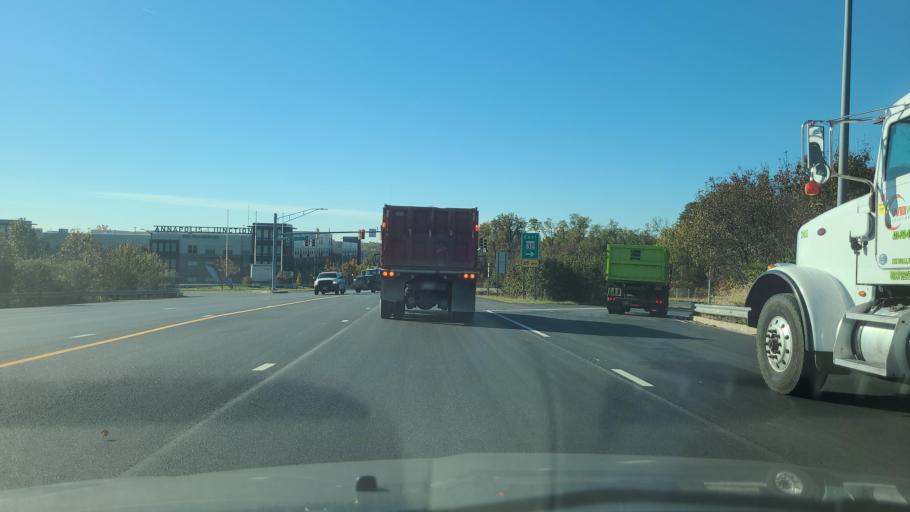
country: US
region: Maryland
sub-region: Howard County
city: Fort George G Mead Junction
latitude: 39.1275
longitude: -76.7955
